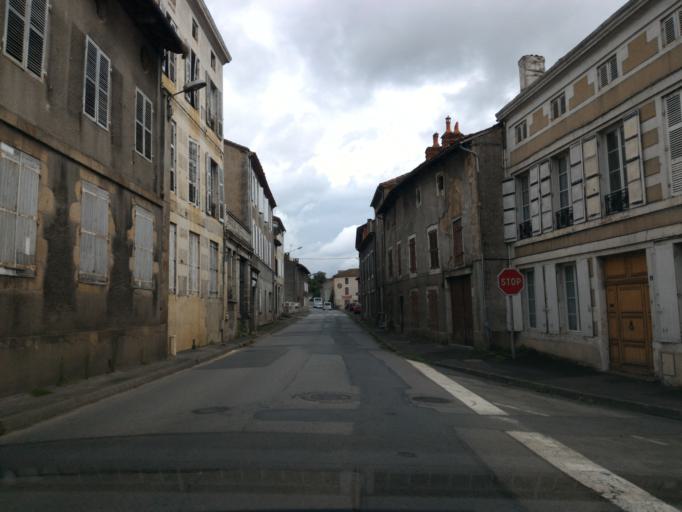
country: FR
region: Poitou-Charentes
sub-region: Departement de la Charente
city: Chabanais
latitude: 45.8766
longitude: 0.7207
